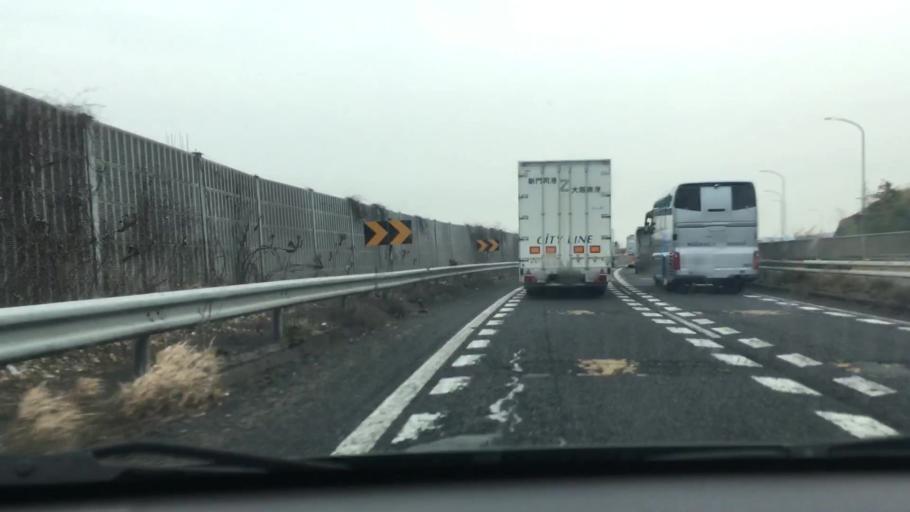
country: JP
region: Mie
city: Ueno-ebisumachi
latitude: 34.7892
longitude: 136.1609
